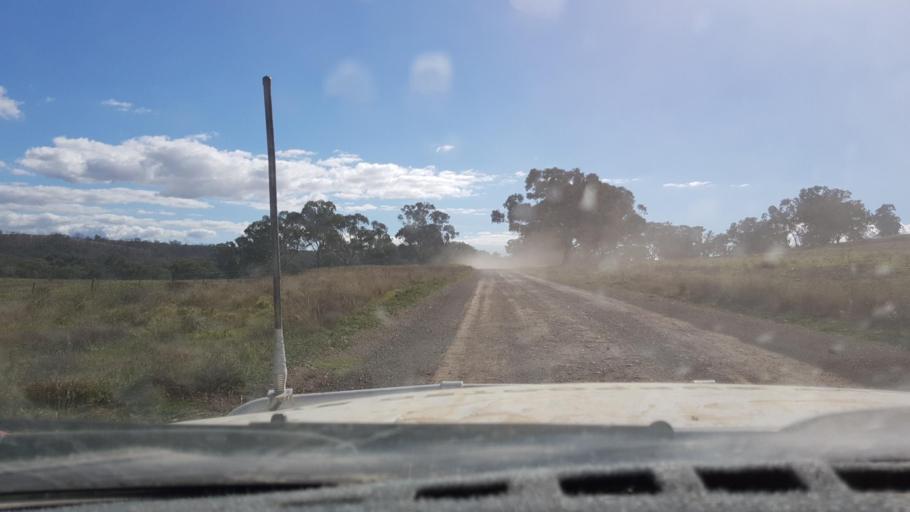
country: AU
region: New South Wales
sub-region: Narrabri
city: Blair Athol
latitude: -30.4308
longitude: 150.4573
